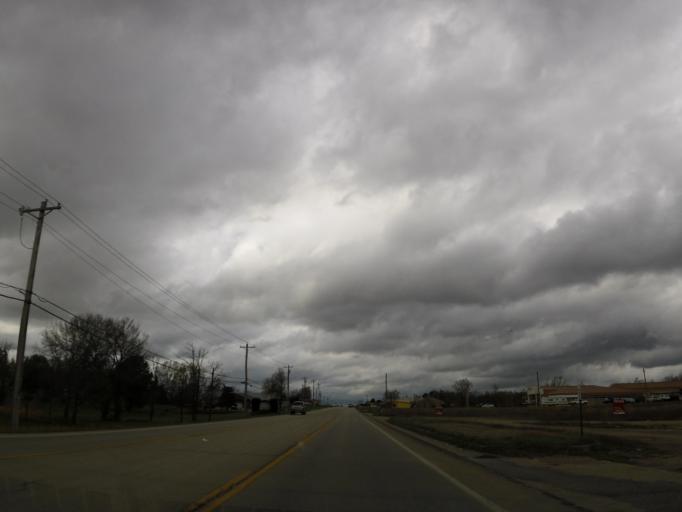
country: US
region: Missouri
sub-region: Butler County
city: Poplar Bluff
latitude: 36.7336
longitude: -90.4327
